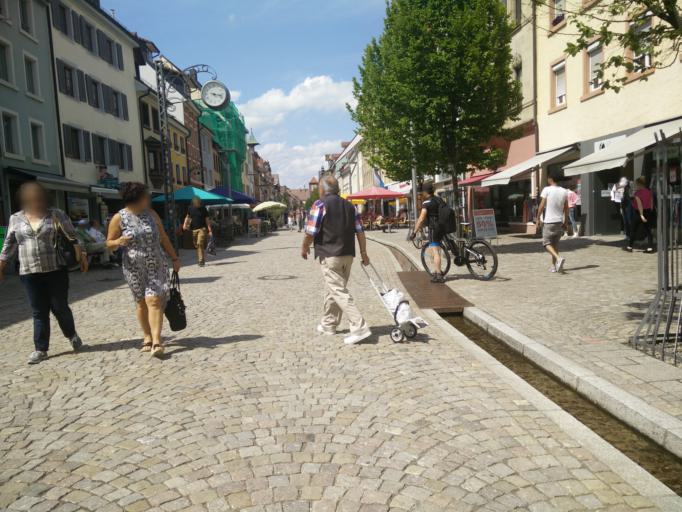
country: DE
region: Baden-Wuerttemberg
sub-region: Freiburg Region
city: Villingen-Schwenningen
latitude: 48.0573
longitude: 8.4609
